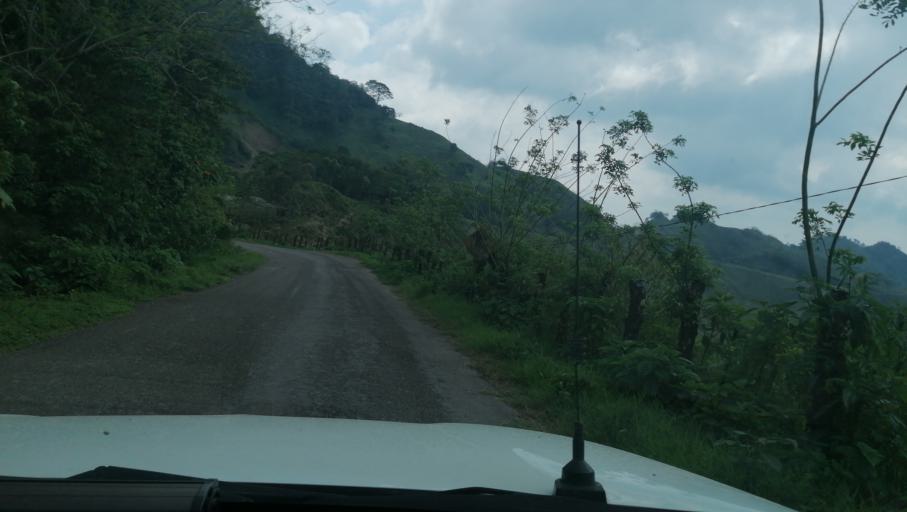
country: MX
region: Chiapas
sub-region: Francisco Leon
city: San Miguel la Sardina
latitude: 17.2424
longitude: -93.2993
